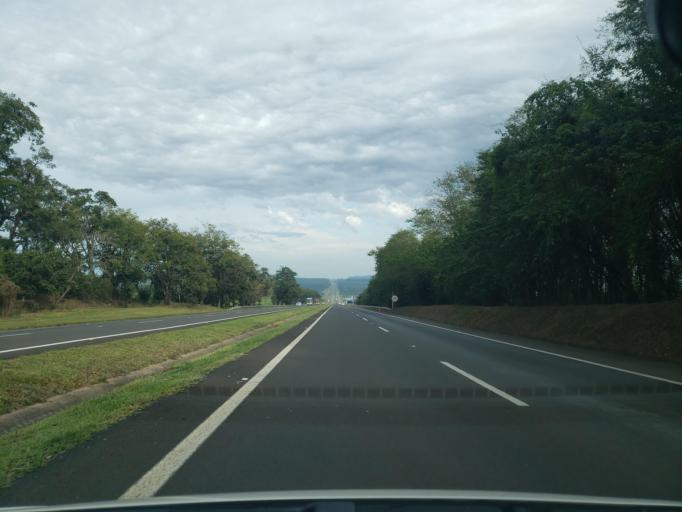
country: BR
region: Sao Paulo
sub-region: Itirapina
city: Itirapina
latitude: -22.2556
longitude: -47.8478
